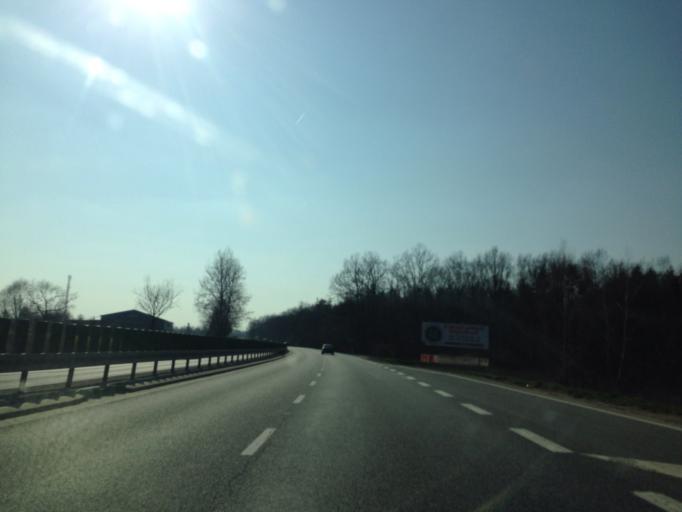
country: PL
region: Lower Silesian Voivodeship
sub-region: Powiat wroclawski
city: Dlugoleka
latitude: 51.1830
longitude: 17.2108
